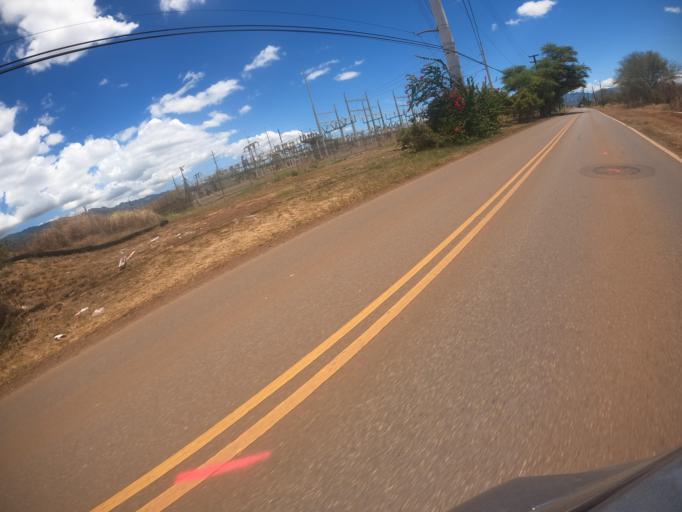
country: US
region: Hawaii
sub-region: Honolulu County
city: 'Ewa Villages
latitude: 21.3709
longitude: -158.0461
